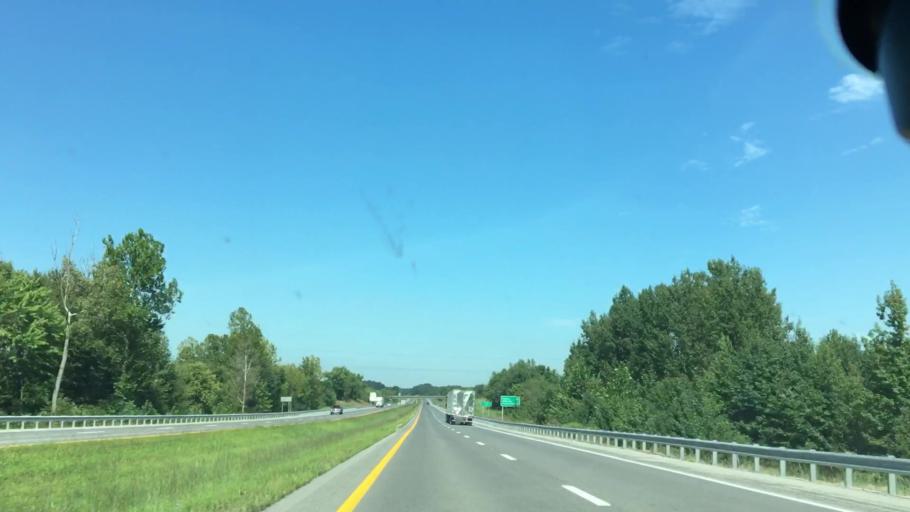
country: US
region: Kentucky
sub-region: Webster County
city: Sebree
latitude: 37.5021
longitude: -87.4750
